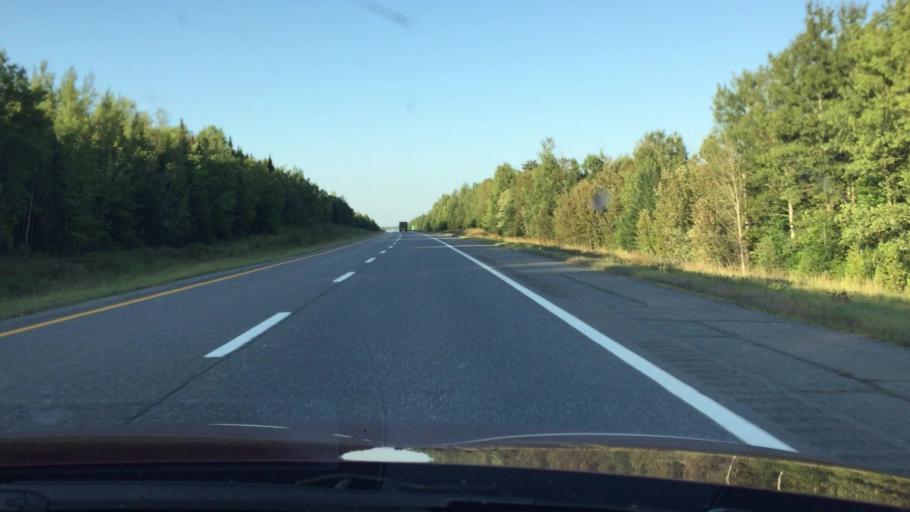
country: US
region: Maine
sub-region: Aroostook County
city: Hodgdon
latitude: 46.1228
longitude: -68.1094
